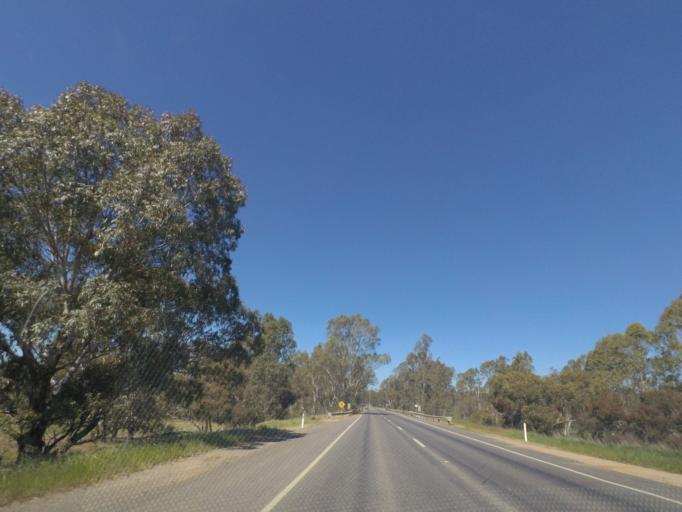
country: AU
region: Victoria
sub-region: Murrindindi
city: Kinglake West
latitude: -37.0299
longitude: 145.0950
